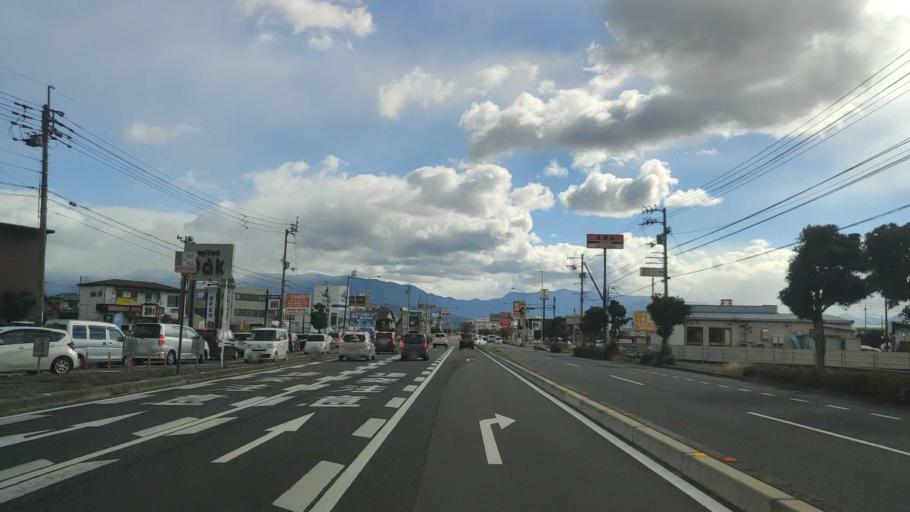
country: JP
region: Ehime
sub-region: Shikoku-chuo Shi
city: Matsuyama
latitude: 33.8154
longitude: 132.7949
